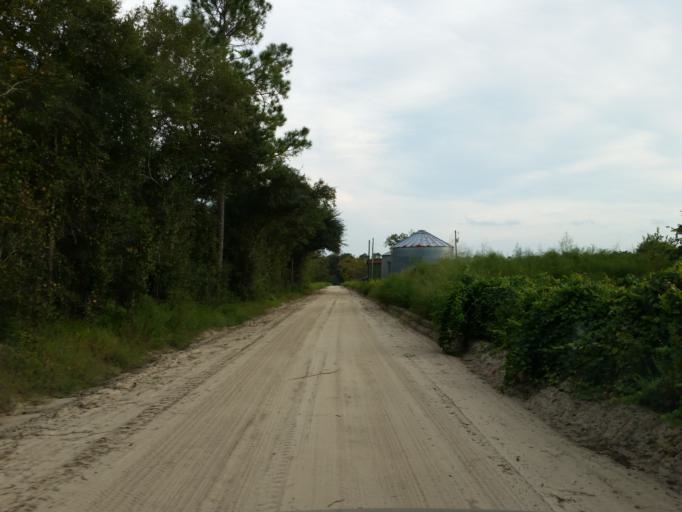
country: US
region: Georgia
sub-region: Echols County
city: Statenville
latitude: 30.5897
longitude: -83.1318
